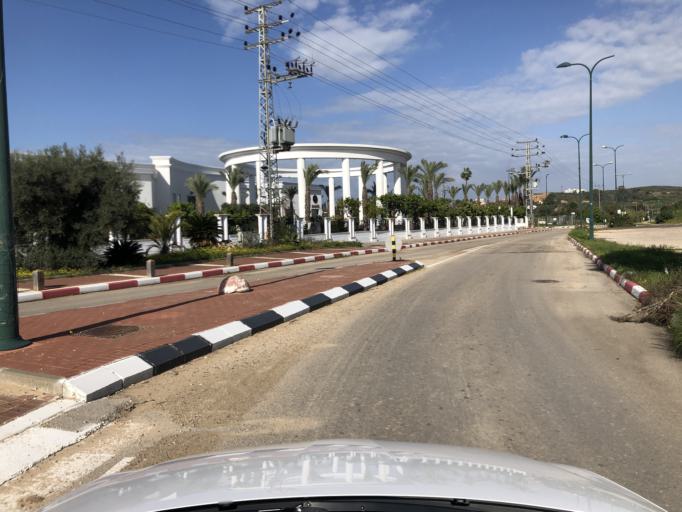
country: IL
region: Central District
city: Ness Ziona
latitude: 31.9149
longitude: 34.7790
